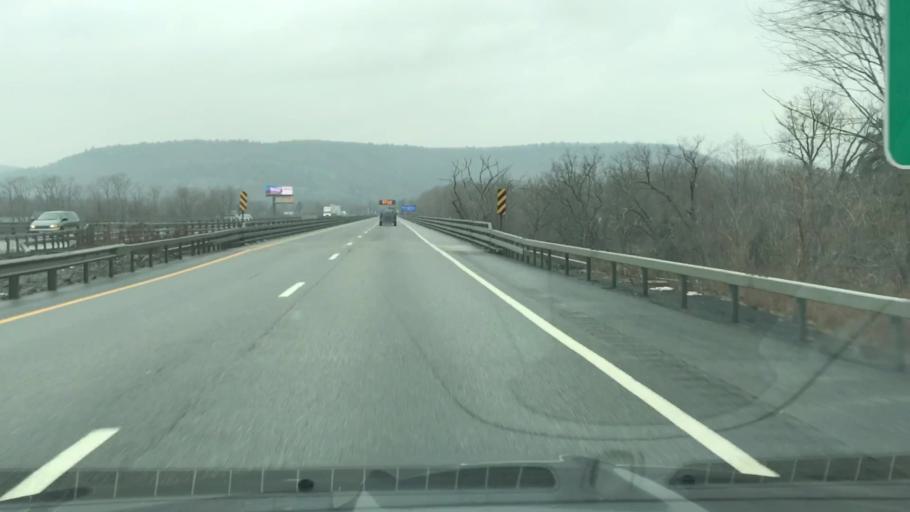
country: US
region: Pennsylvania
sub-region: Pike County
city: Matamoras
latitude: 41.3570
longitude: -74.6929
